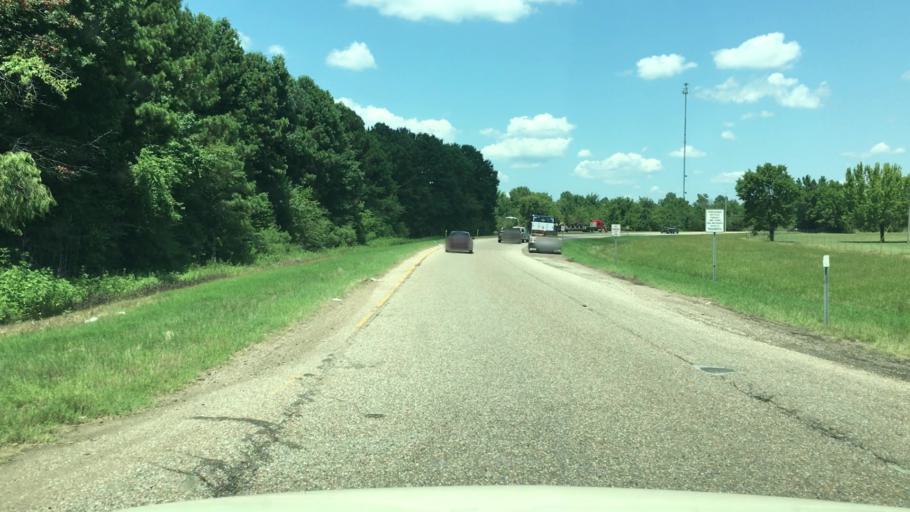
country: US
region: Arkansas
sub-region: Nevada County
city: Prescott
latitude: 33.8106
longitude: -93.4203
